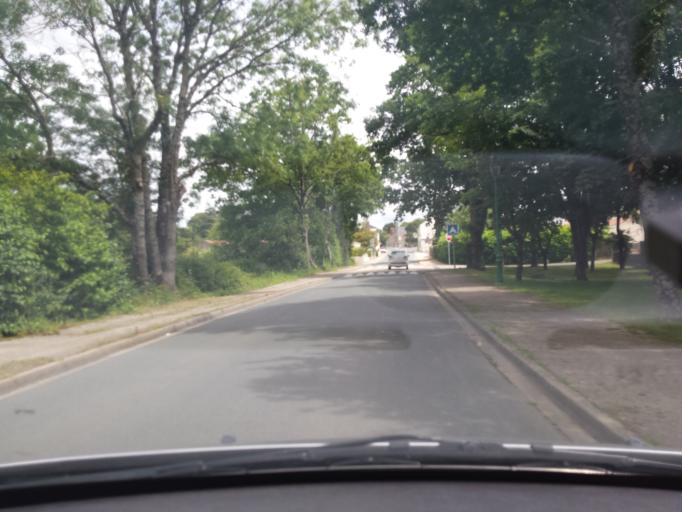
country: FR
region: Pays de la Loire
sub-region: Departement de la Vendee
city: Landeronde
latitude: 46.6596
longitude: -1.5756
